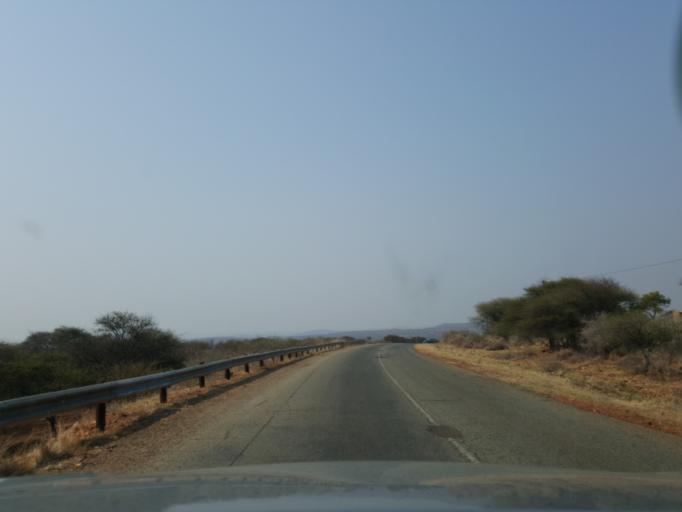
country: ZA
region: North-West
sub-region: Ngaka Modiri Molema District Municipality
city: Zeerust
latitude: -25.3271
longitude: 25.9396
